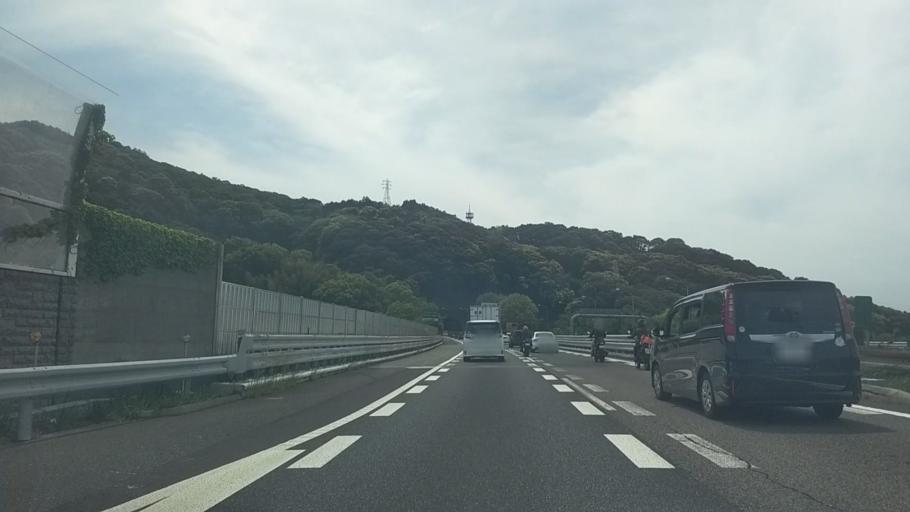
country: JP
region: Shizuoka
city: Kosai-shi
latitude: 34.8151
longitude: 137.5522
